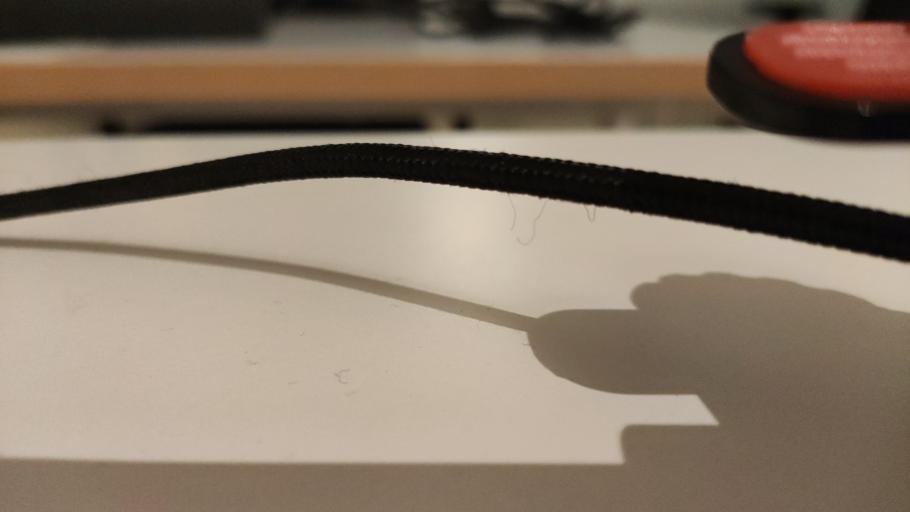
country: RU
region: Moskovskaya
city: Il'inskiy Pogost
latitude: 55.5159
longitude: 38.8716
